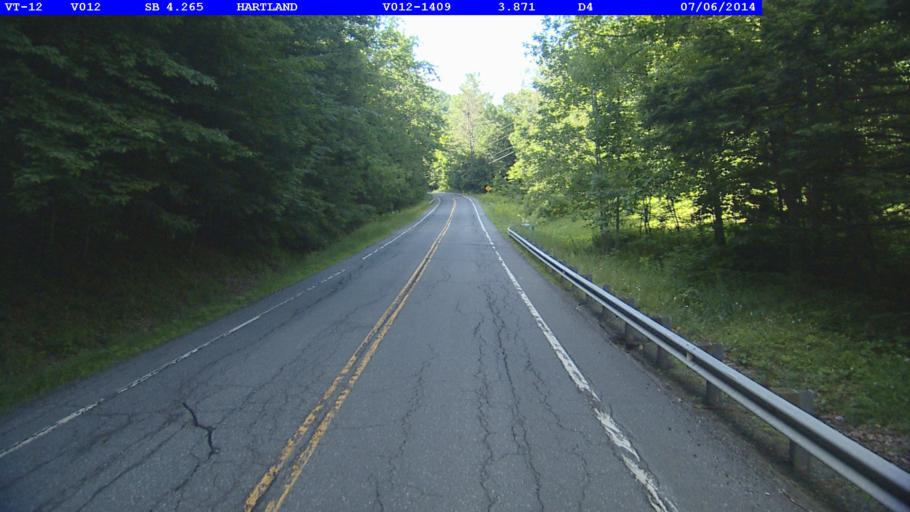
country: US
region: Vermont
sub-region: Windsor County
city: Woodstock
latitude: 43.5745
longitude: -72.4434
